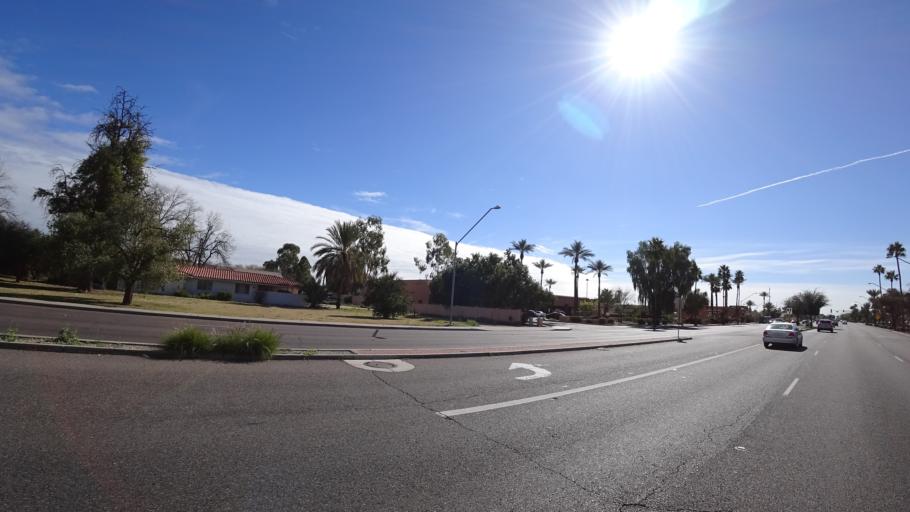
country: US
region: Arizona
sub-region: Maricopa County
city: Glendale
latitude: 33.5842
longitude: -112.1862
